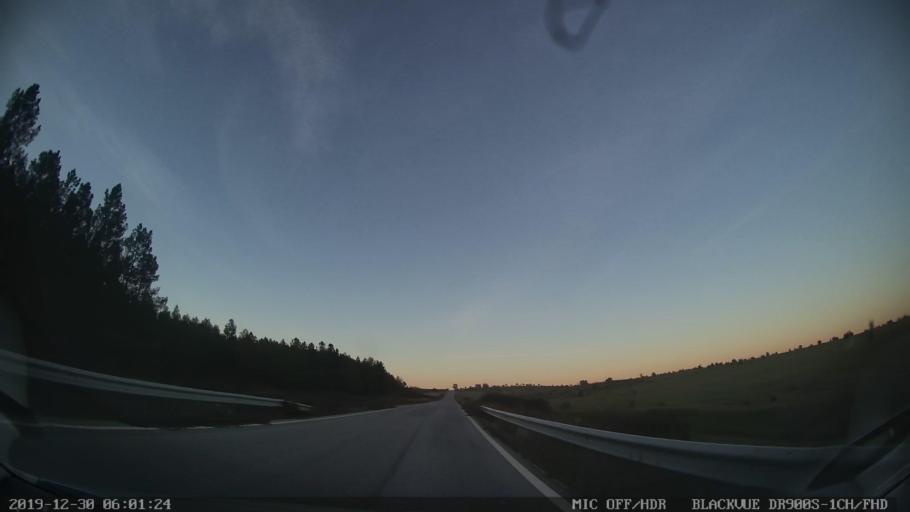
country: PT
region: Castelo Branco
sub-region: Penamacor
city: Penamacor
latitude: 40.0604
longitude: -7.2434
